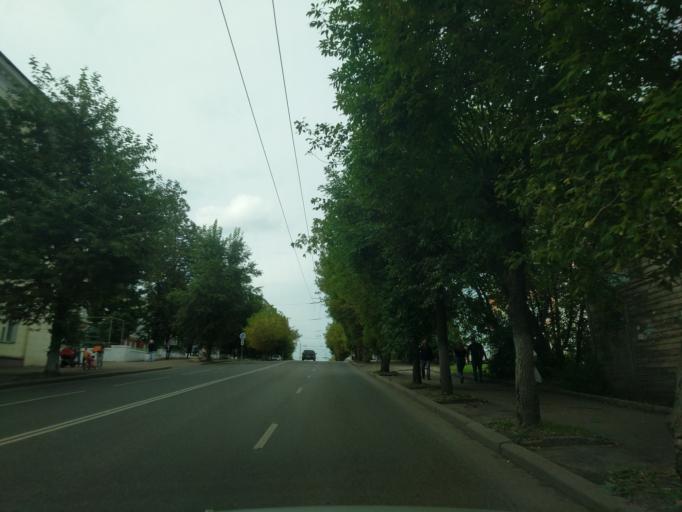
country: RU
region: Kirov
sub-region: Kirovo-Chepetskiy Rayon
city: Kirov
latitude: 58.5919
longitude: 49.6689
